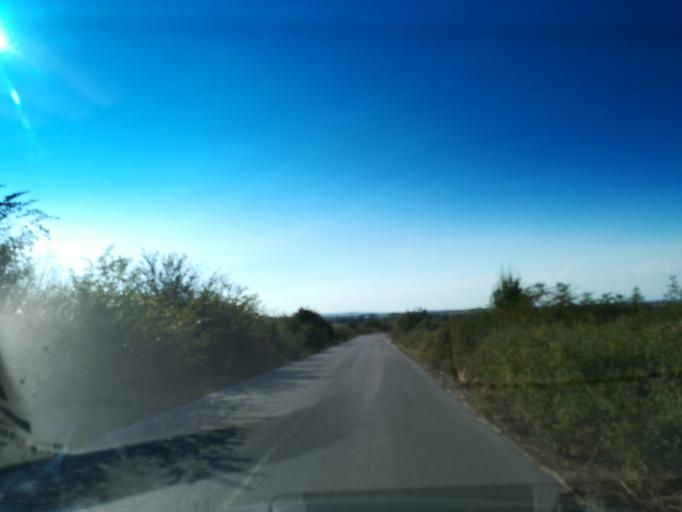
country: BG
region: Khaskovo
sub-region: Obshtina Mineralni Bani
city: Mineralni Bani
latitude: 42.0484
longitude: 25.2756
